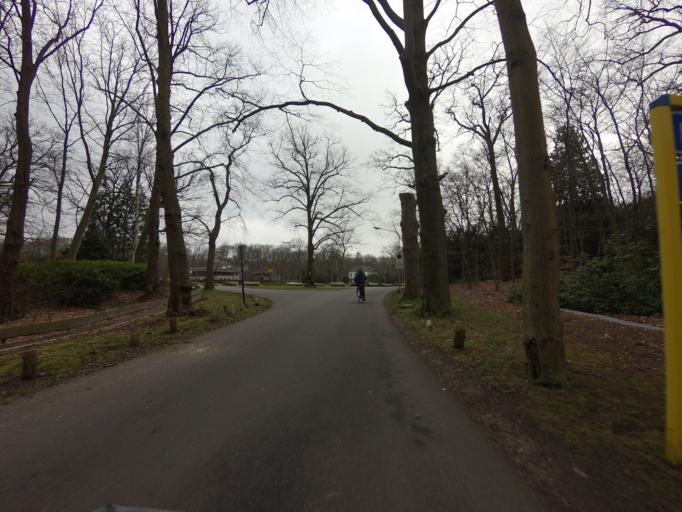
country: NL
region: North Holland
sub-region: Gemeente Wijdemeren
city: Kortenhoef
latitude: 52.2394
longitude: 5.1422
